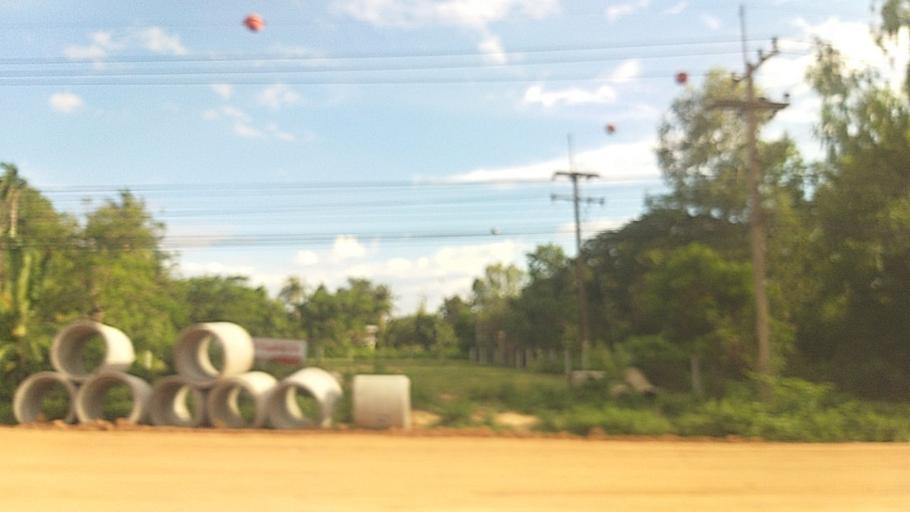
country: TH
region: Surin
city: Kap Choeng
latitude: 14.4729
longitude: 103.6070
